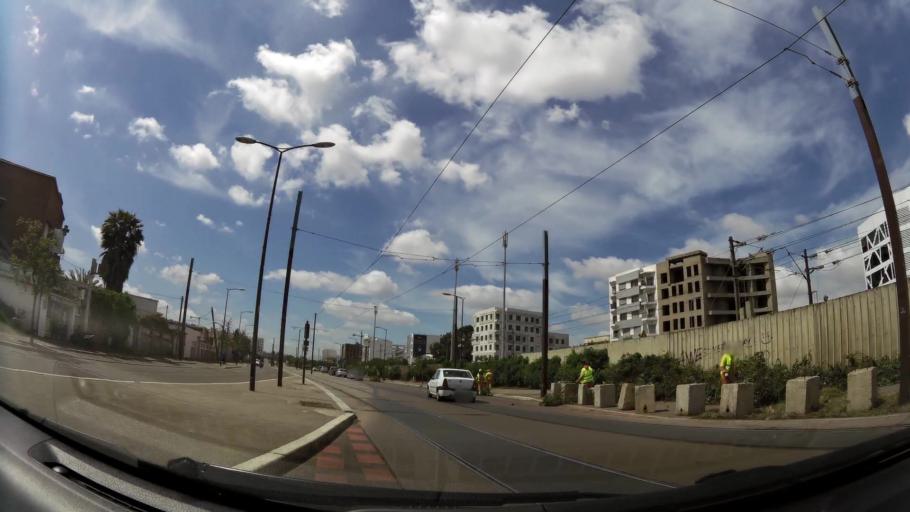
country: MA
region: Grand Casablanca
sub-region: Casablanca
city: Casablanca
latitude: 33.5600
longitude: -7.6289
